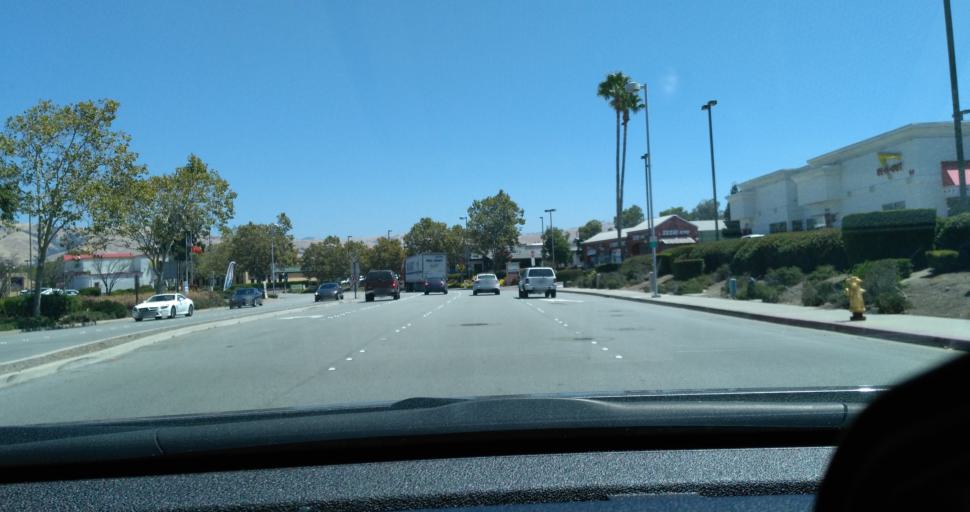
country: US
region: California
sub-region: Santa Clara County
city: Milpitas
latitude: 37.4265
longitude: -121.9231
